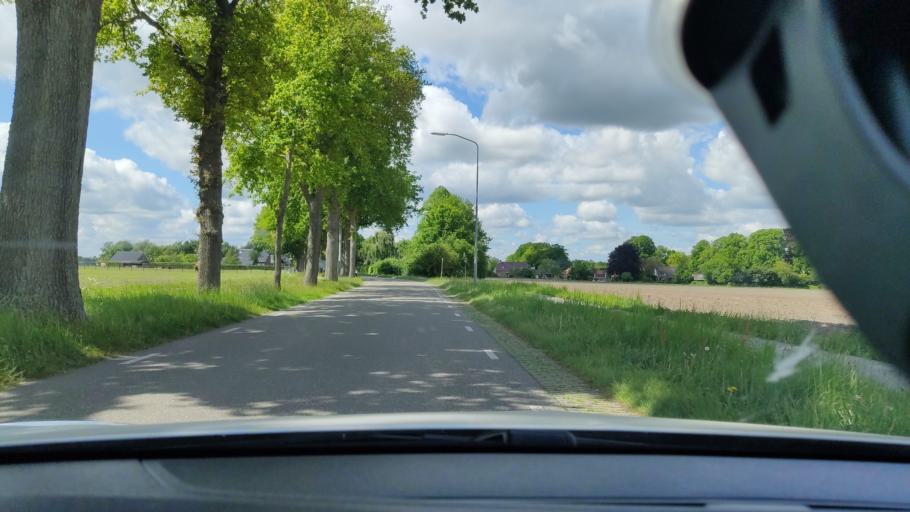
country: NL
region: Drenthe
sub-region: Gemeente Tynaarlo
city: Zuidlaren
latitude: 53.1158
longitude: 6.6715
